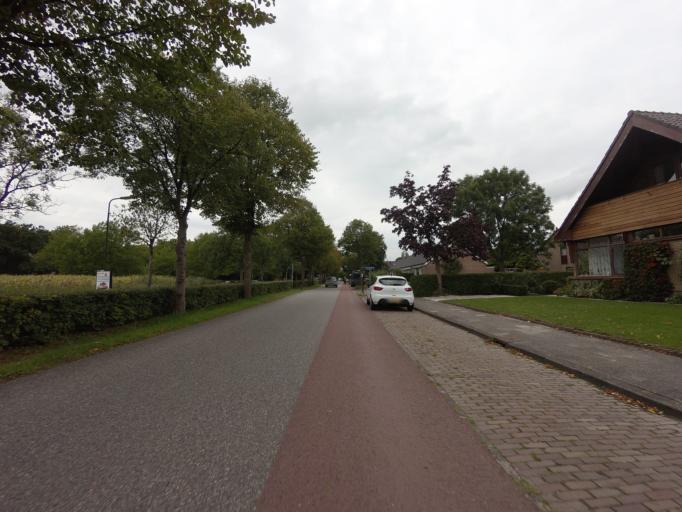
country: NL
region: Friesland
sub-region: Sudwest Fryslan
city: Sneek
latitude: 53.0406
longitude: 5.6354
